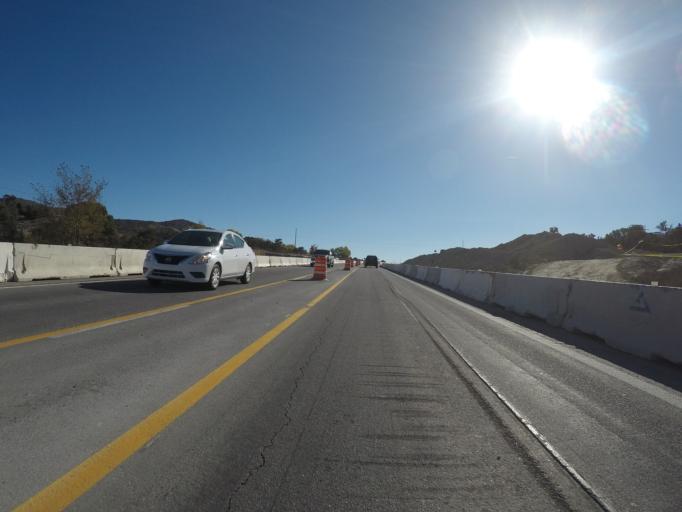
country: US
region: Nevada
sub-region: Clark County
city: Summerlin South
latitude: 36.0179
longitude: -115.5062
